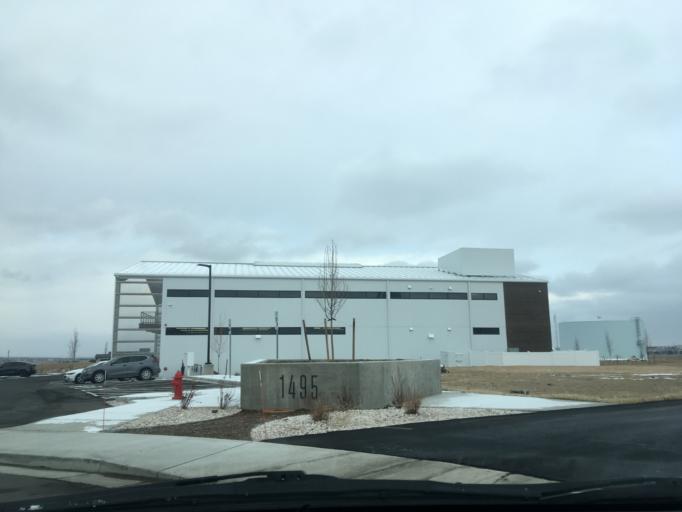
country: US
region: Colorado
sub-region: Boulder County
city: Lafayette
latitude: 39.9767
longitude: -105.0651
